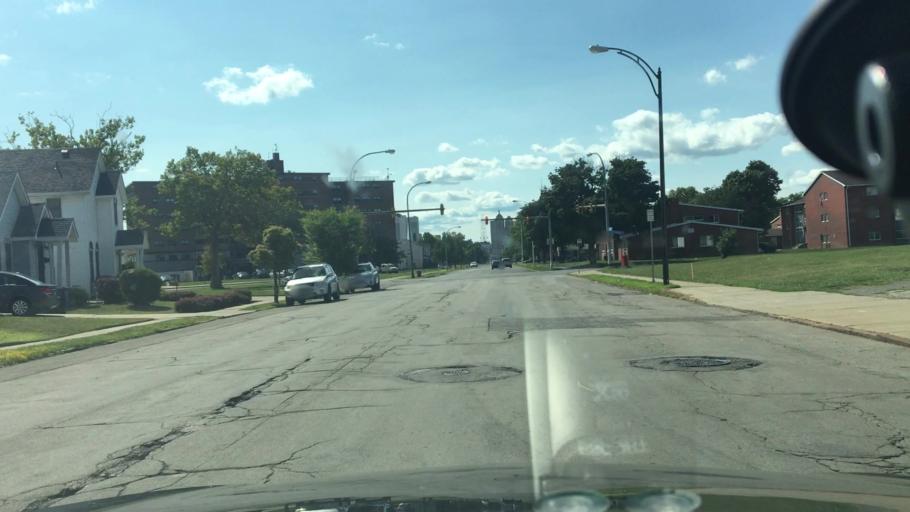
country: US
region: New York
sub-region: Erie County
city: Buffalo
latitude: 42.8817
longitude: -78.8530
